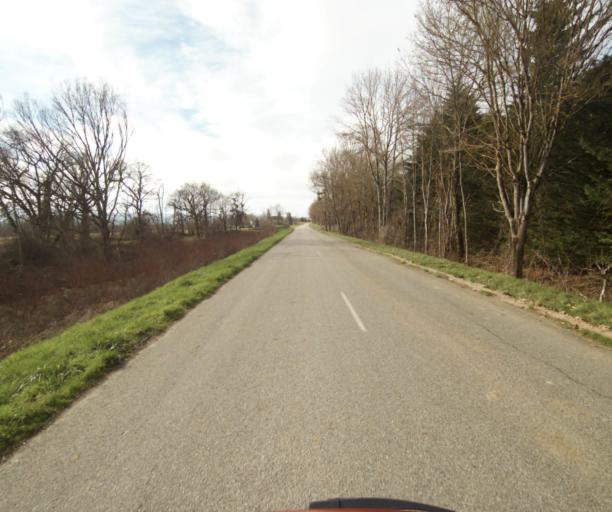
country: FR
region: Midi-Pyrenees
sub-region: Departement de l'Ariege
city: Pamiers
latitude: 43.1316
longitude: 1.5548
